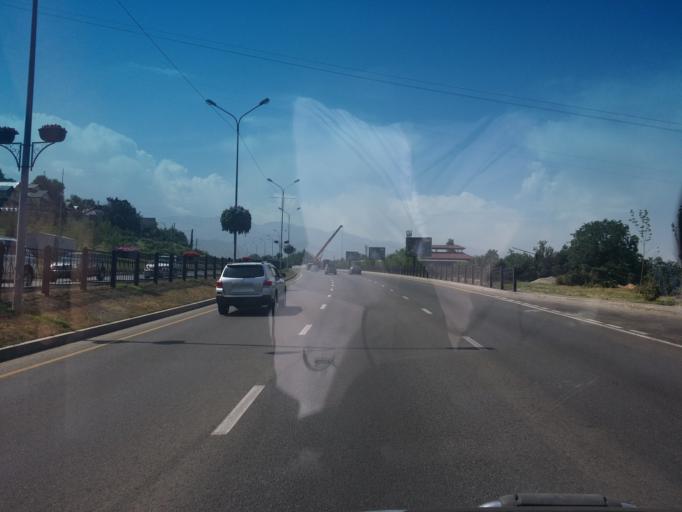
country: KZ
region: Almaty Qalasy
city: Almaty
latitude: 43.2384
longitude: 76.9714
